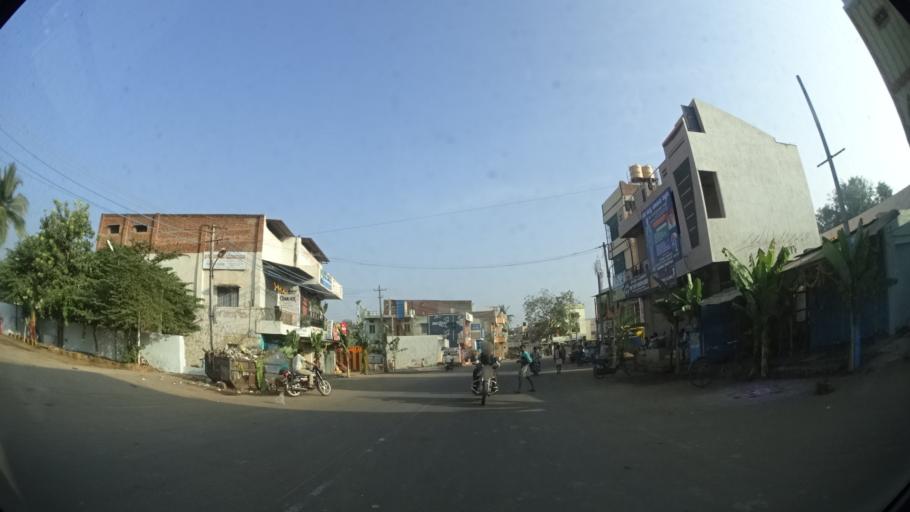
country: IN
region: Karnataka
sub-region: Bellary
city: Hospet
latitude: 15.2691
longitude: 76.3889
